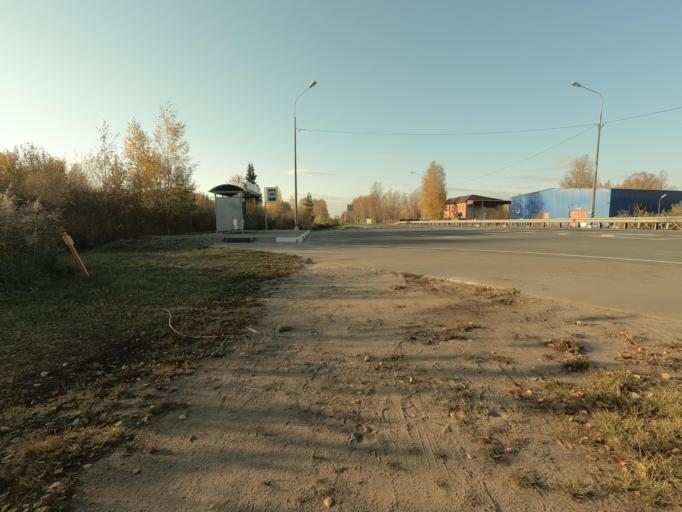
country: RU
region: Leningrad
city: Kirovsk
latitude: 59.8558
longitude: 31.0131
